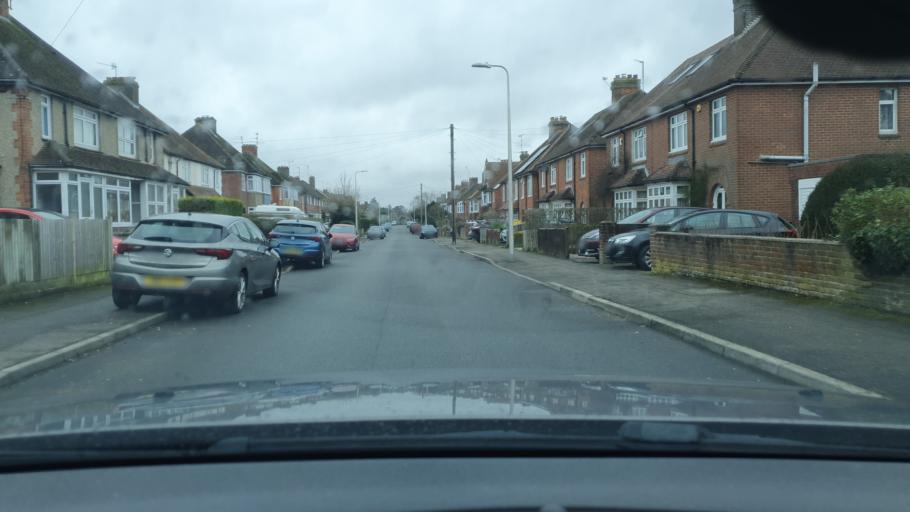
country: GB
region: England
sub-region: West Berkshire
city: Greenham
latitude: 51.3873
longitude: -1.3232
